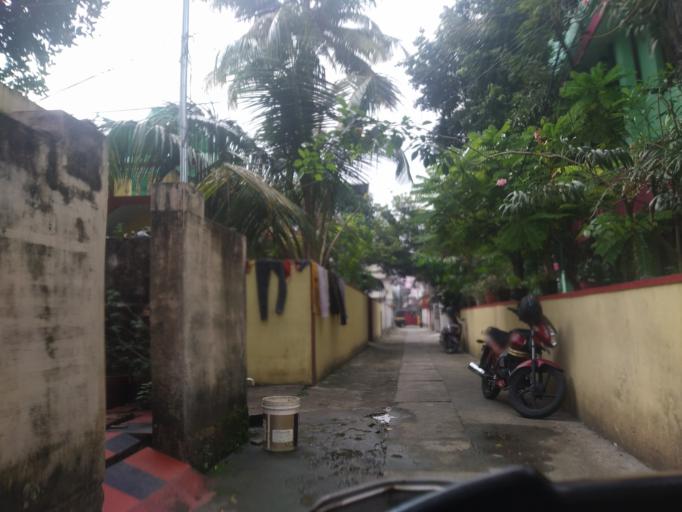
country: IN
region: Kerala
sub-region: Ernakulam
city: Cochin
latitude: 9.9811
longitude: 76.2886
